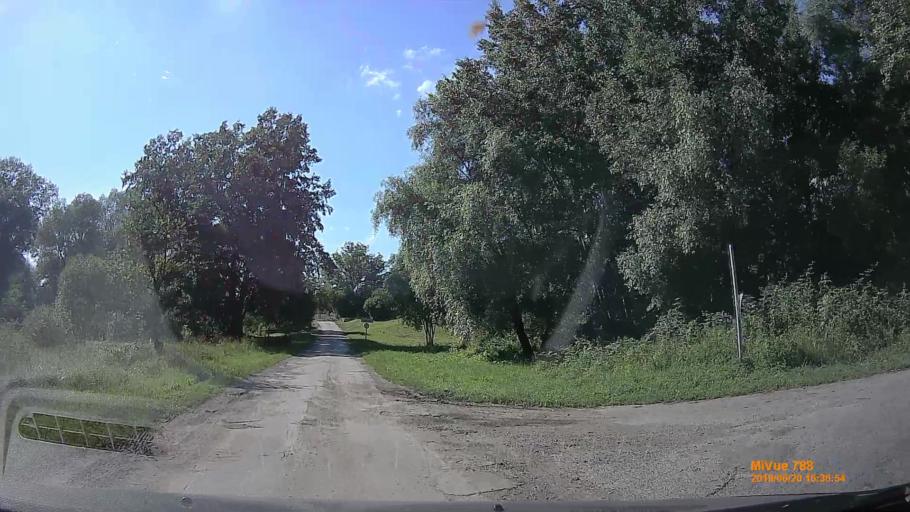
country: HU
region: Baranya
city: Buekkoesd
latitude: 46.1712
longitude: 18.0523
